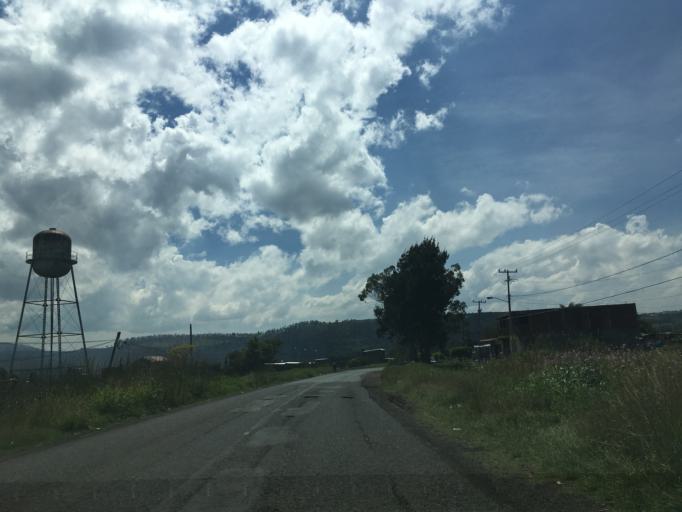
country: MX
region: Michoacan
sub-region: Morelia
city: La Mintzita (Piedra Dura)
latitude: 19.6565
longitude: -101.2797
